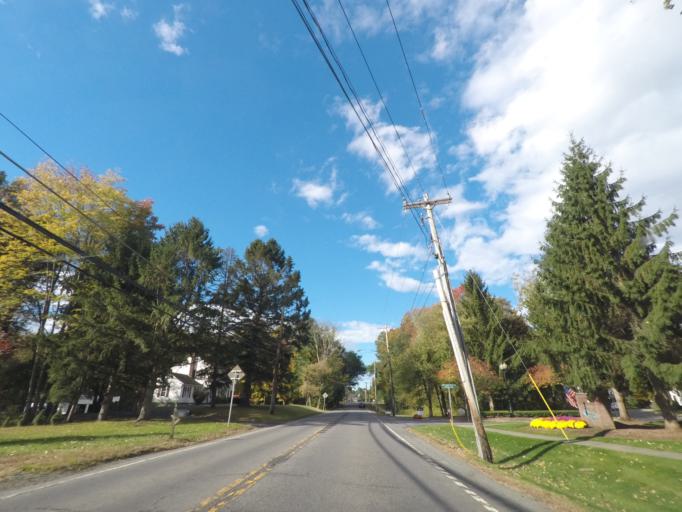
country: US
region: New York
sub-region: Schenectady County
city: Rotterdam
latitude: 42.7372
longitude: -73.9405
